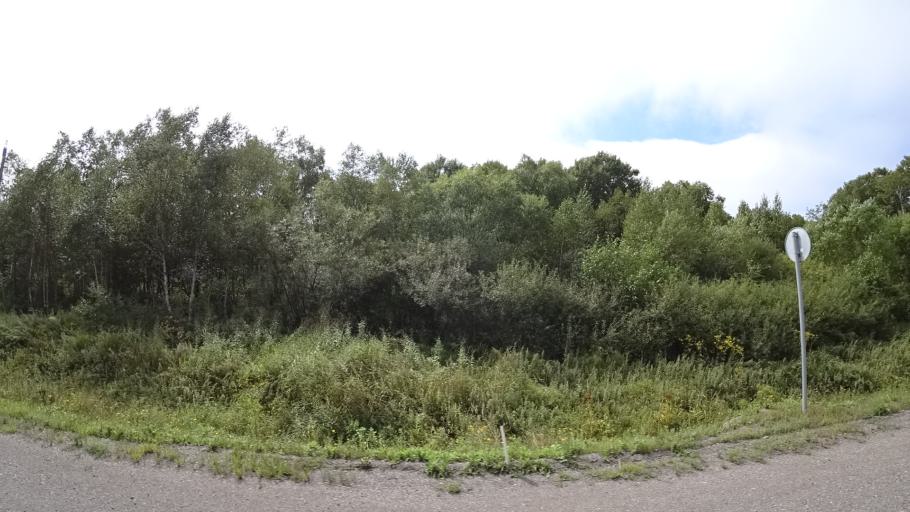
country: RU
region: Primorskiy
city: Lyalichi
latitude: 44.1092
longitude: 132.4201
